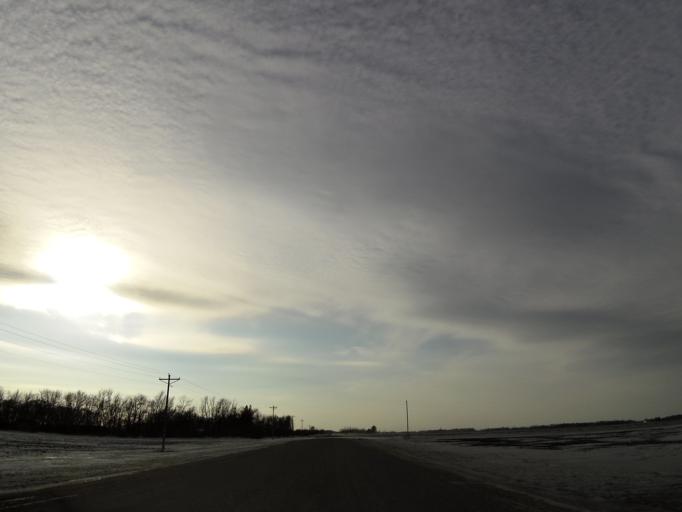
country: US
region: North Dakota
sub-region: Walsh County
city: Grafton
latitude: 48.4269
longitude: -97.3298
